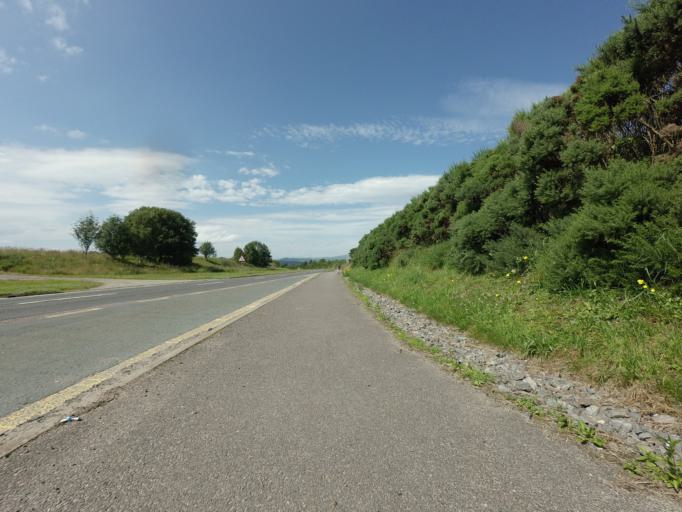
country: GB
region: Scotland
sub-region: Highland
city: Conon Bridge
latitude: 57.5492
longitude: -4.3933
